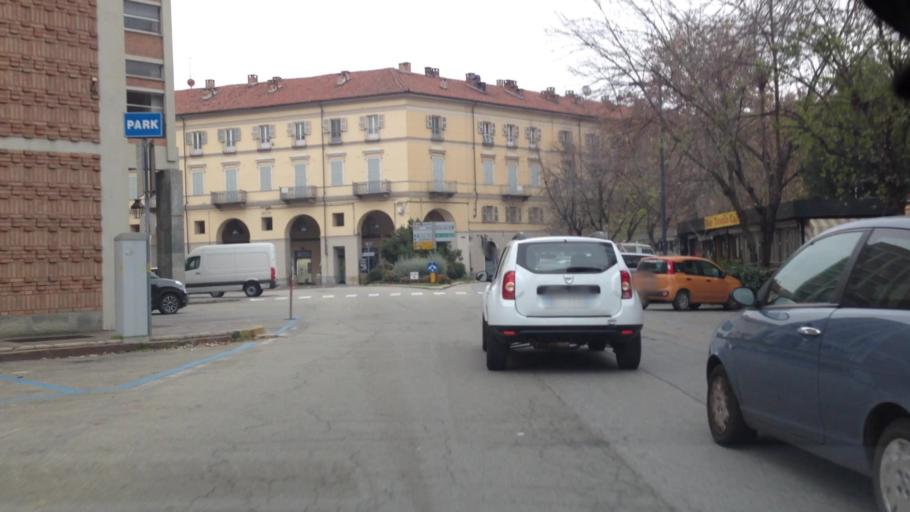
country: IT
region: Piedmont
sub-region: Provincia di Asti
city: Asti
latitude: 44.8991
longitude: 8.2084
